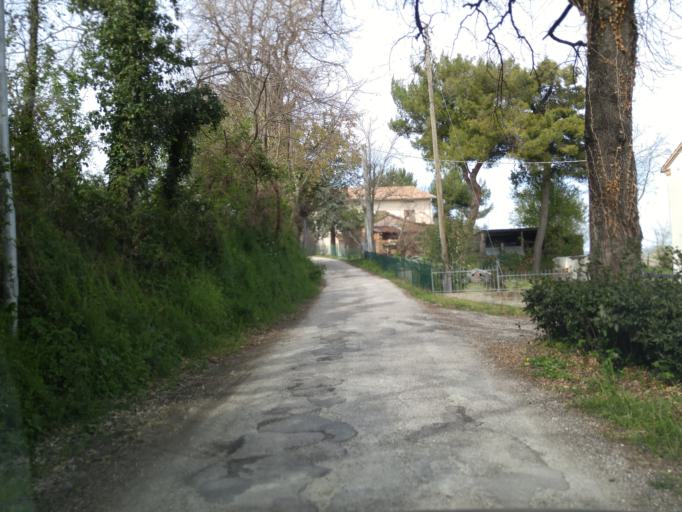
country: IT
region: The Marches
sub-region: Provincia di Pesaro e Urbino
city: Cartoceto
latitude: 43.7684
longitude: 12.8959
